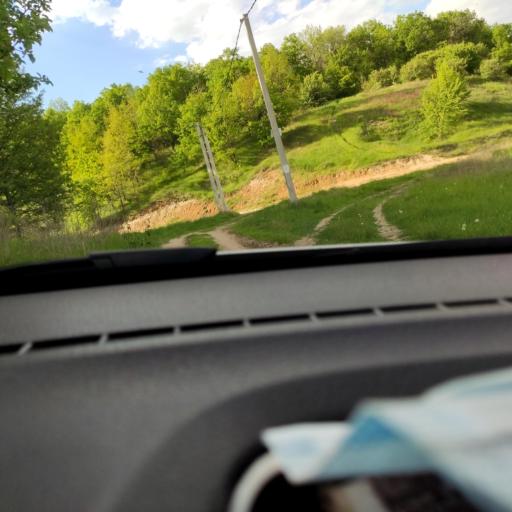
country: RU
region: Voronezj
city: Ramon'
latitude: 51.9390
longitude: 39.3715
